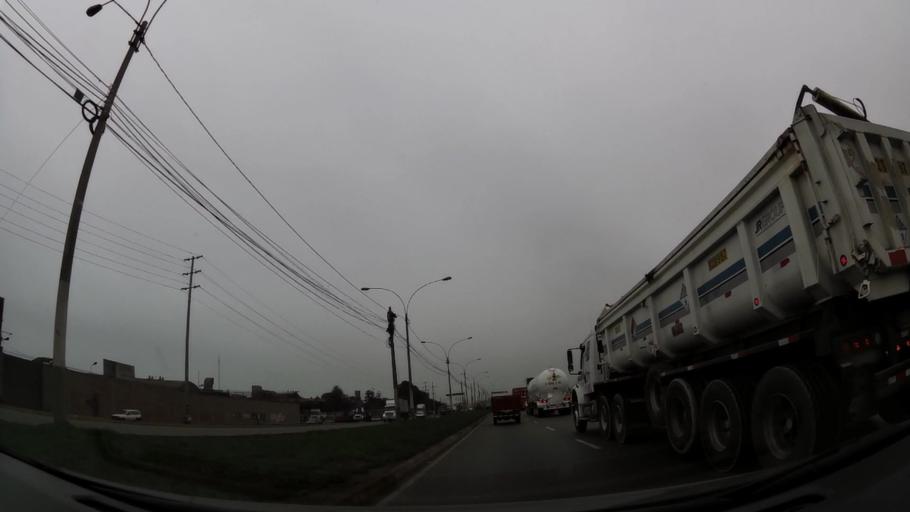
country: PE
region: Callao
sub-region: Callao
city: Callao
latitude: -11.9870
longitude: -77.1255
